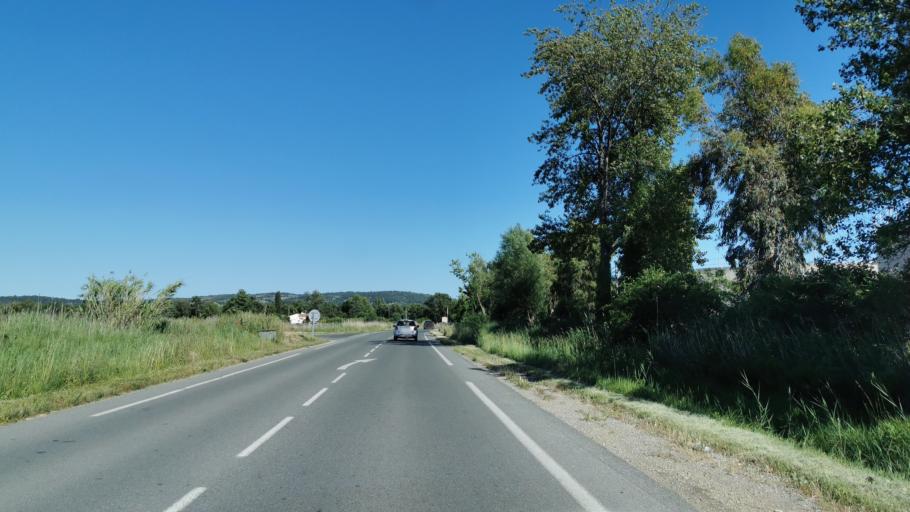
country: FR
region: Languedoc-Roussillon
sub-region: Departement de l'Aude
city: Narbonne
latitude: 43.1732
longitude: 3.0307
